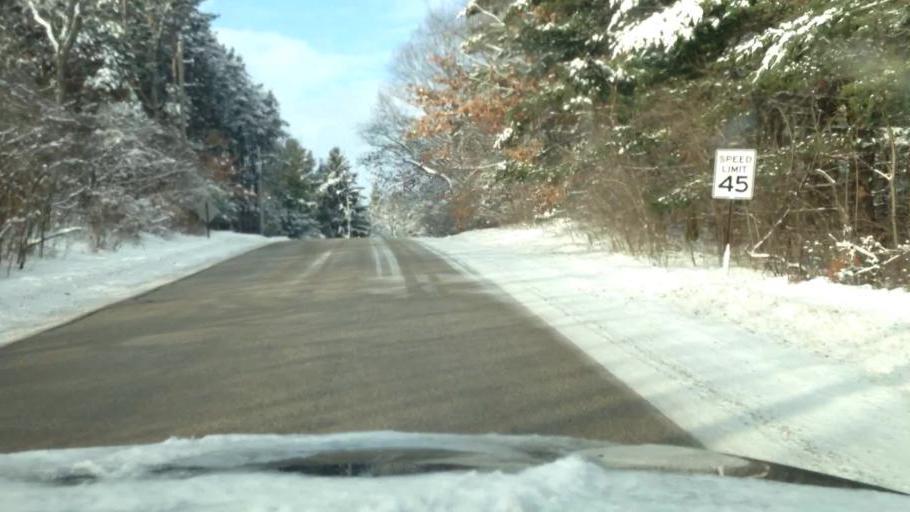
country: US
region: Wisconsin
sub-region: Walworth County
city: East Troy
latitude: 42.8112
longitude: -88.4267
